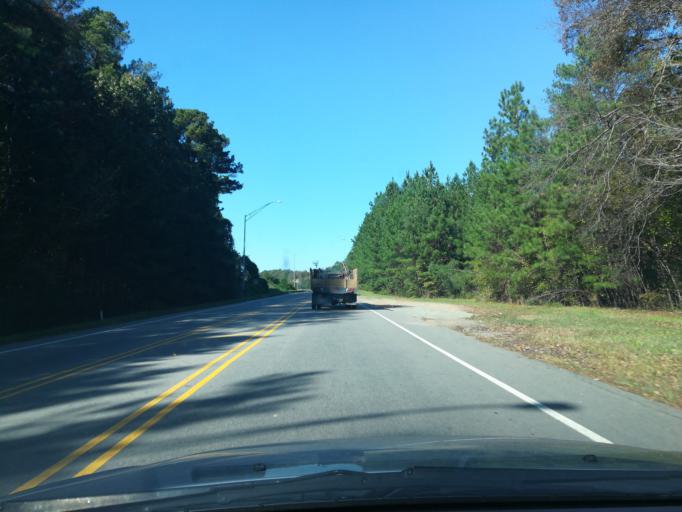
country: US
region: North Carolina
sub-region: Durham County
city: Durham
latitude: 36.0266
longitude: -78.9582
